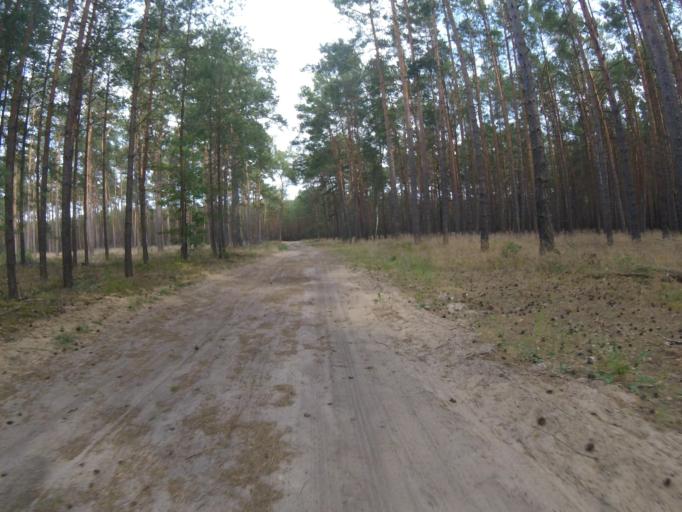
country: DE
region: Brandenburg
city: Wildau
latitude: 52.3171
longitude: 13.7353
